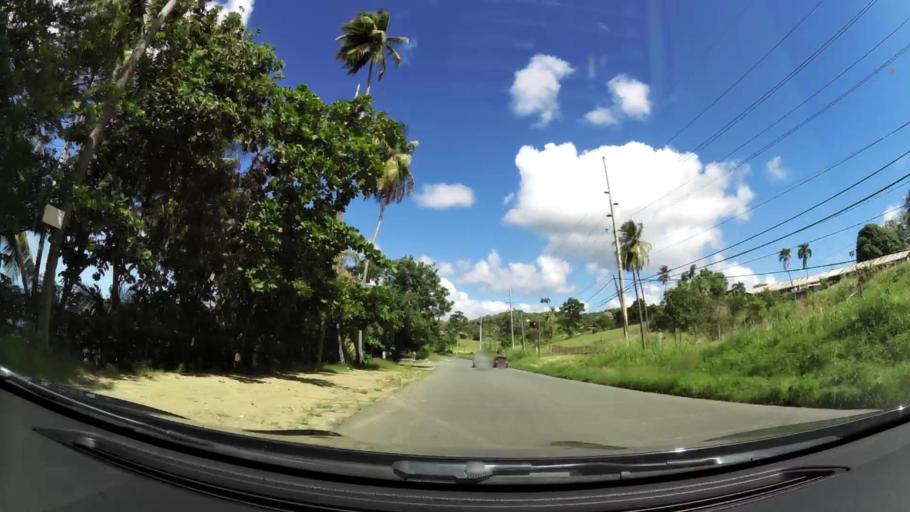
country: TT
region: Tobago
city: Scarborough
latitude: 11.1867
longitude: -60.7976
